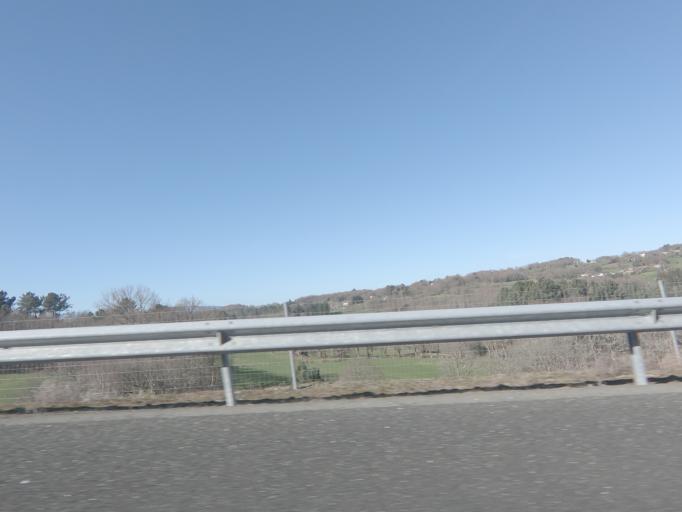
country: ES
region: Galicia
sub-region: Provincia de Pontevedra
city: Lalin
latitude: 42.6112
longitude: -8.1007
